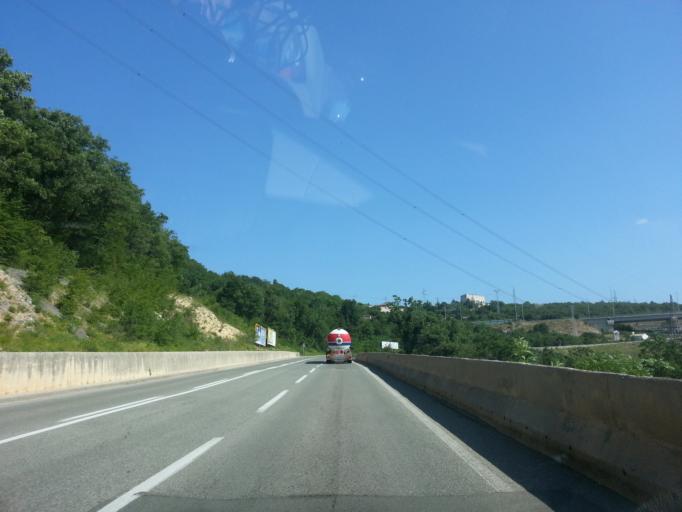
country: HR
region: Primorsko-Goranska
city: Bakar
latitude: 45.3083
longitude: 14.5257
